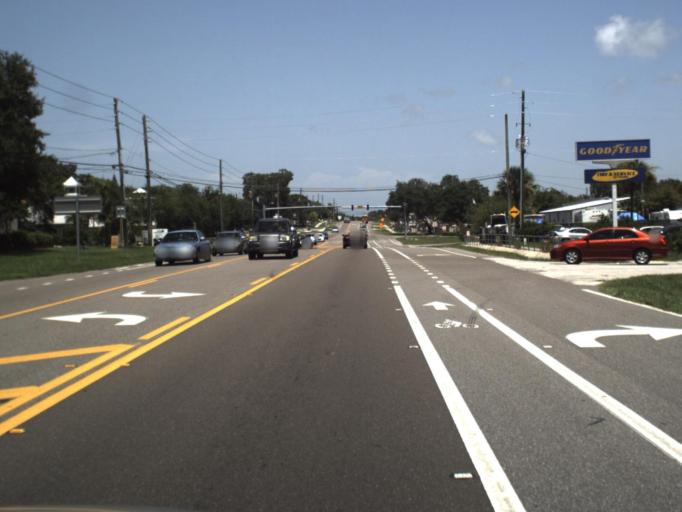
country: US
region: Florida
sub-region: Pinellas County
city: Palm Harbor
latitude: 28.0948
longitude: -82.7726
